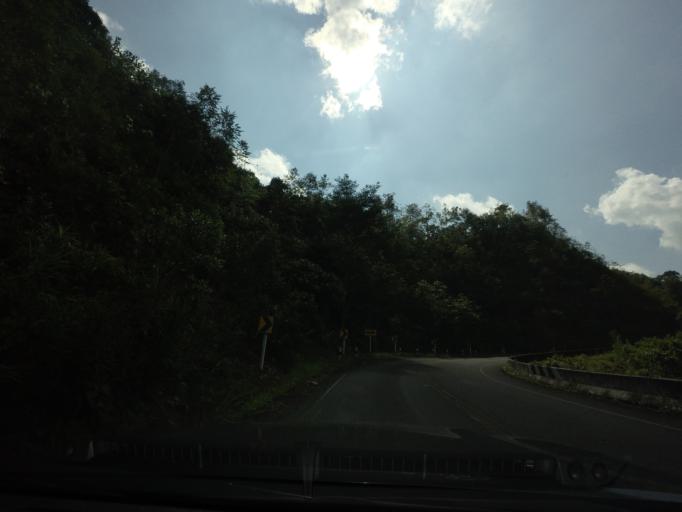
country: TH
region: Nan
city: Bo Kluea
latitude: 19.0689
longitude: 101.1250
